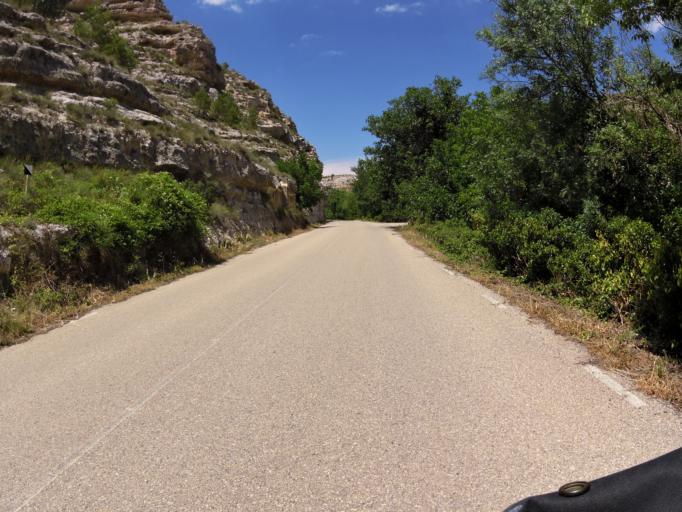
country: ES
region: Castille-La Mancha
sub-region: Provincia de Albacete
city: Jorquera
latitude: 39.1714
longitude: -1.5333
